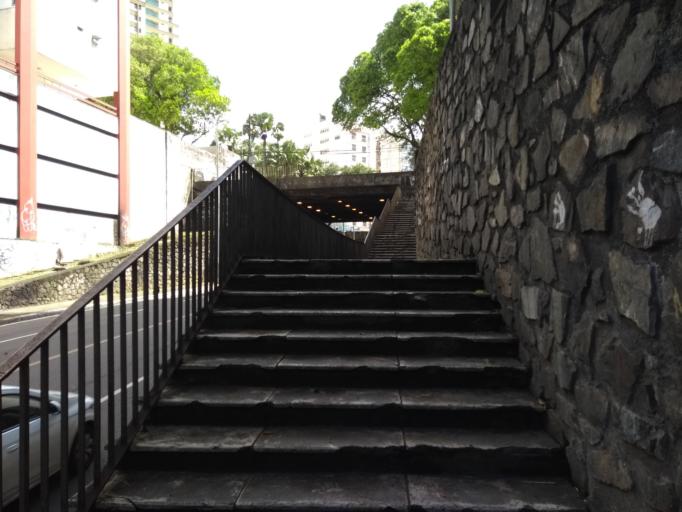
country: BR
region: Bahia
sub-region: Salvador
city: Salvador
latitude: -12.9898
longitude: -38.5230
